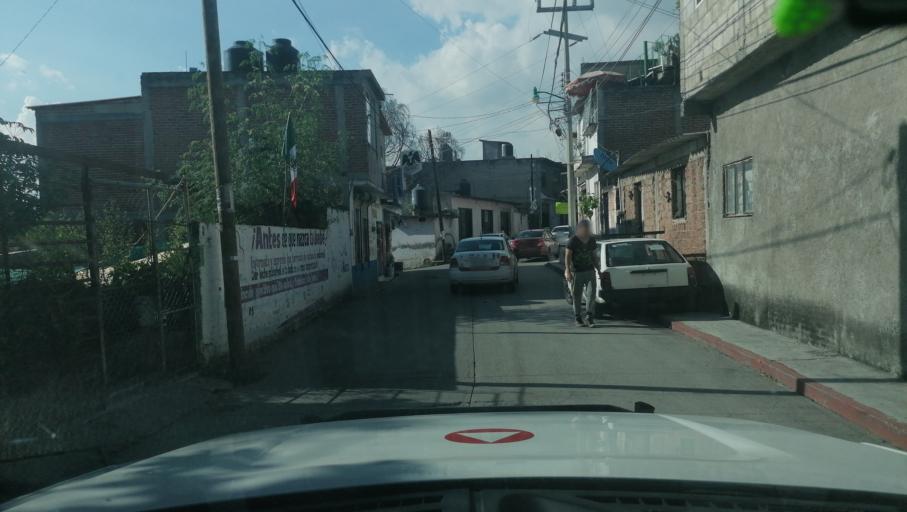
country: MX
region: Morelos
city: Emiliano Zapata
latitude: 18.8404
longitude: -99.1933
